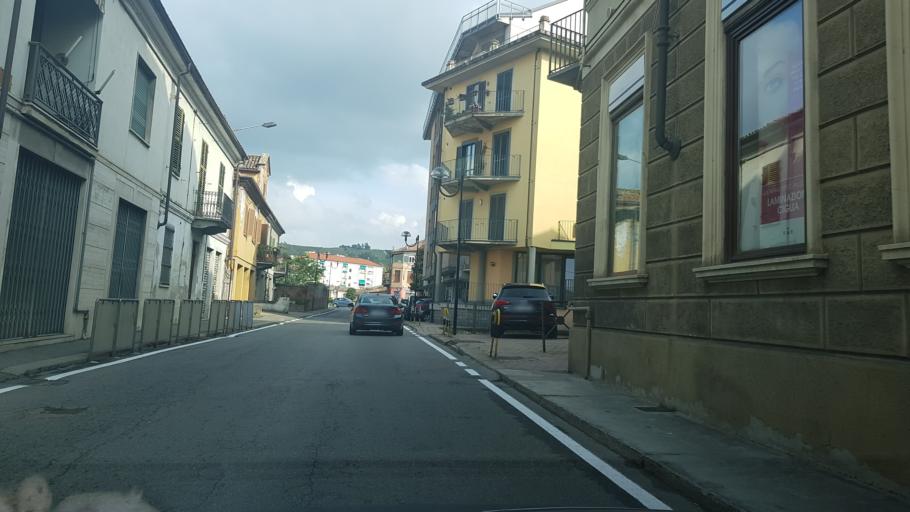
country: IT
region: Piedmont
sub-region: Provincia di Asti
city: Canelli
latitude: 44.7156
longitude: 8.2883
